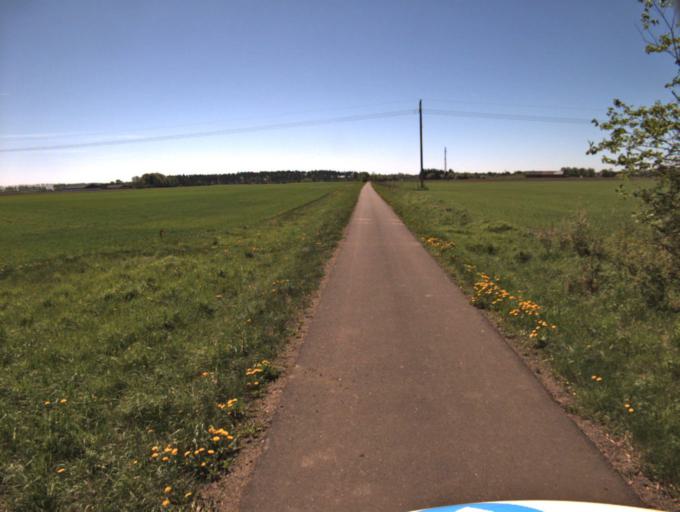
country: SE
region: Skane
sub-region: Kristianstads Kommun
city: Norra Asum
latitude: 55.9611
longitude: 14.1577
